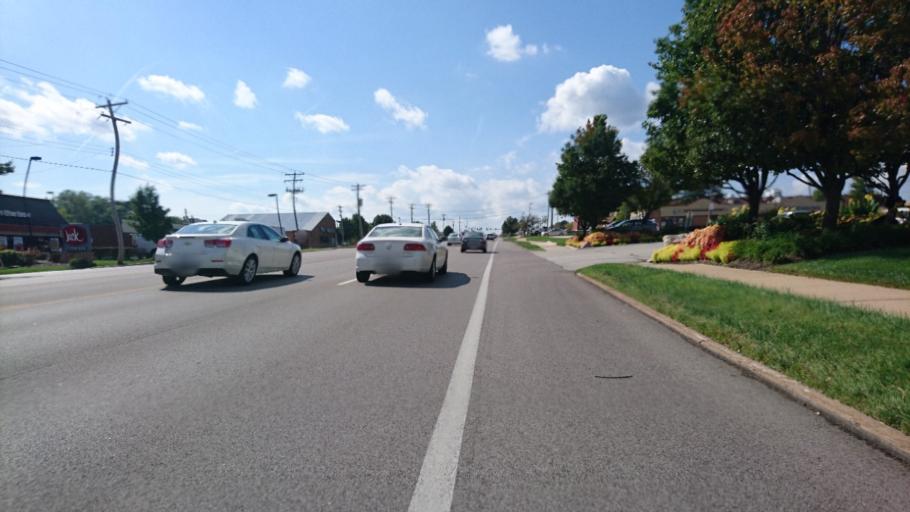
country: US
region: Missouri
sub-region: Saint Louis County
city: Ballwin
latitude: 38.5929
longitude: -90.5601
